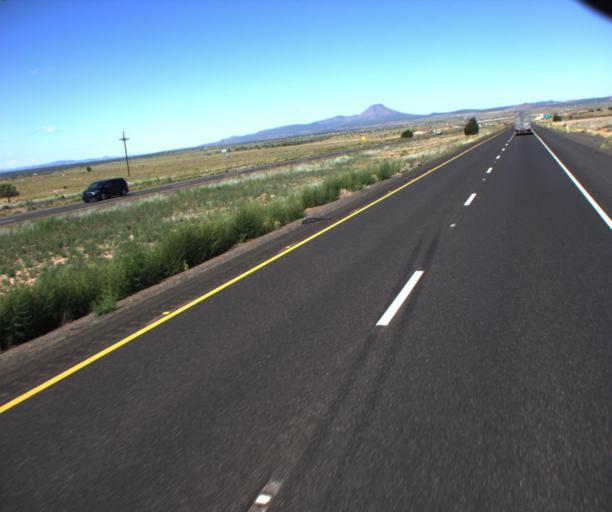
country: US
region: Arizona
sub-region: Yavapai County
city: Paulden
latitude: 35.2279
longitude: -112.5767
